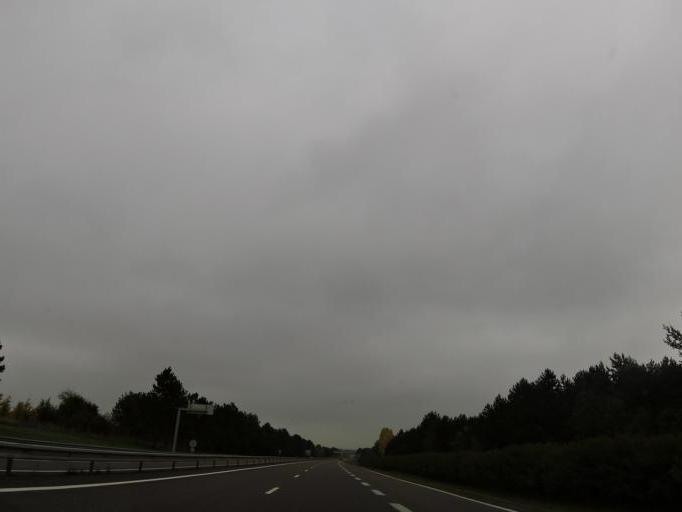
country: FR
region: Champagne-Ardenne
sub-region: Departement de la Marne
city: Courtisols
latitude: 49.0282
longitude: 4.5268
